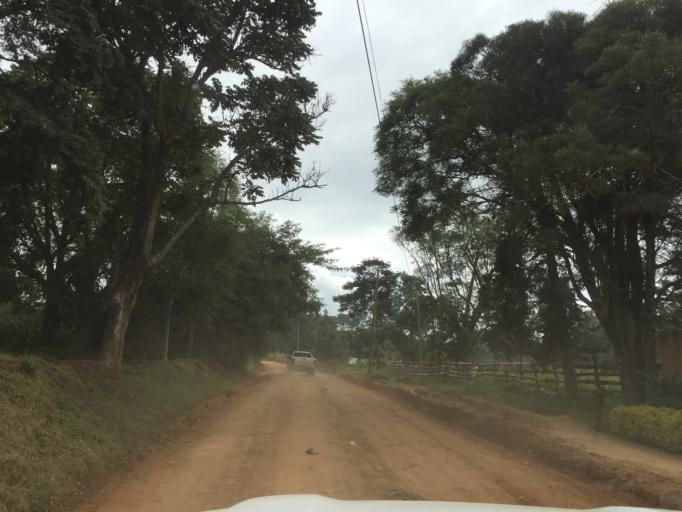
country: TZ
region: Iringa
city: Iringa
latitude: -7.7736
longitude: 35.7080
